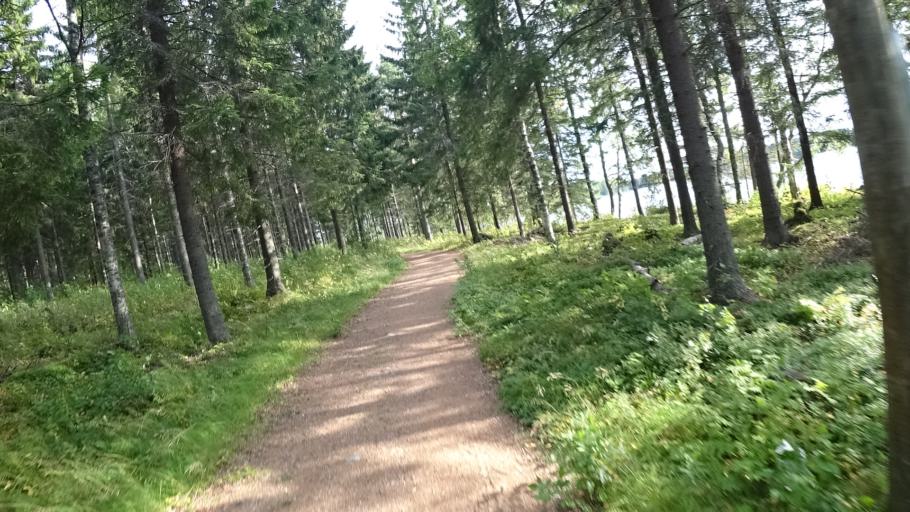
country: FI
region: North Karelia
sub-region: Joensuu
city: Ilomantsi
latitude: 62.6690
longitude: 30.9059
